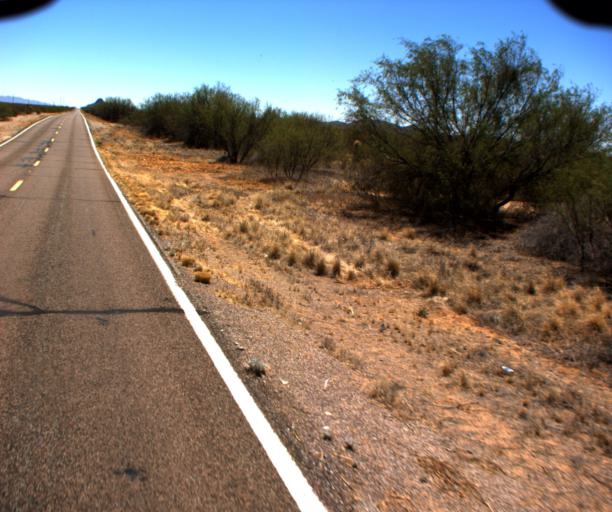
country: US
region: Arizona
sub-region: Pima County
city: Ajo
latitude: 32.2078
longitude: -112.5936
